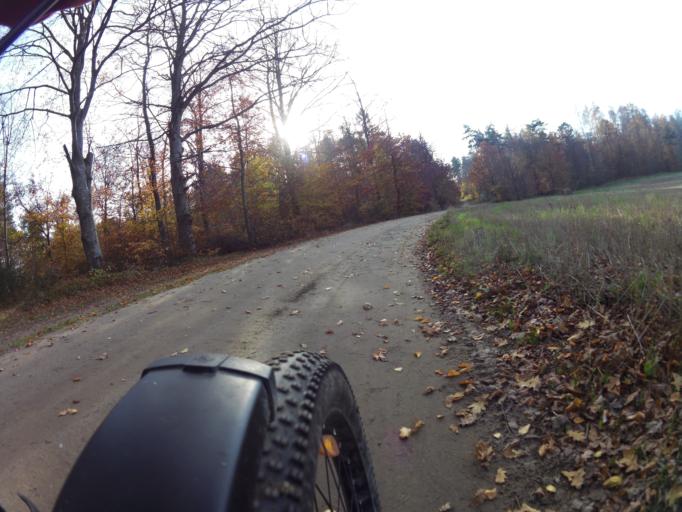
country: PL
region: Pomeranian Voivodeship
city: Strzelno
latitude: 54.7430
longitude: 18.2847
